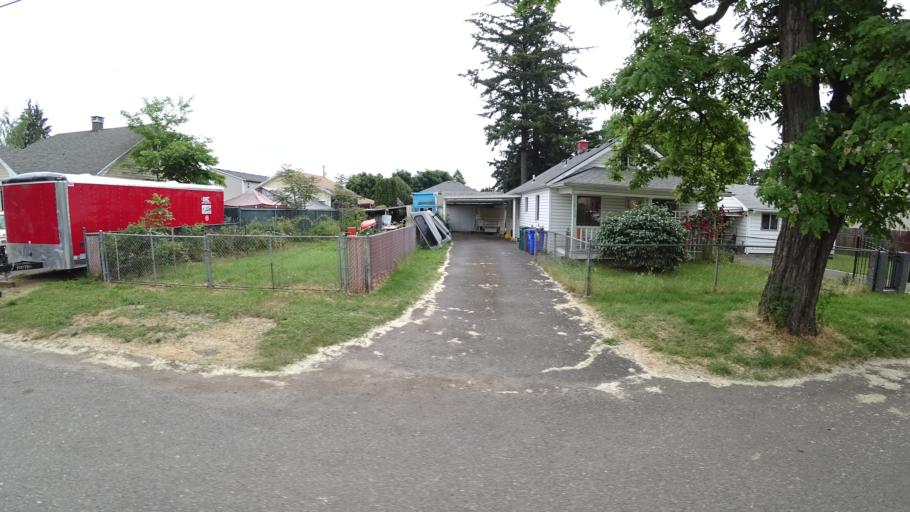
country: US
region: Oregon
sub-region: Multnomah County
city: Lents
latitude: 45.4740
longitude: -122.5840
